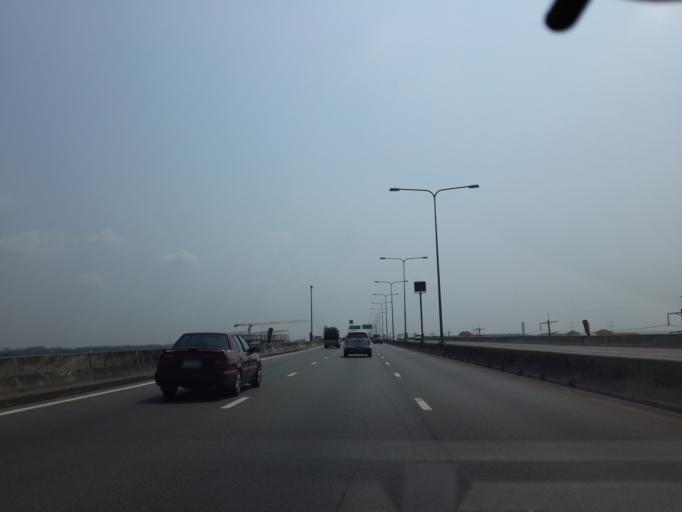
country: TH
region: Samut Prakan
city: Bang Bo
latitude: 13.5785
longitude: 100.8821
